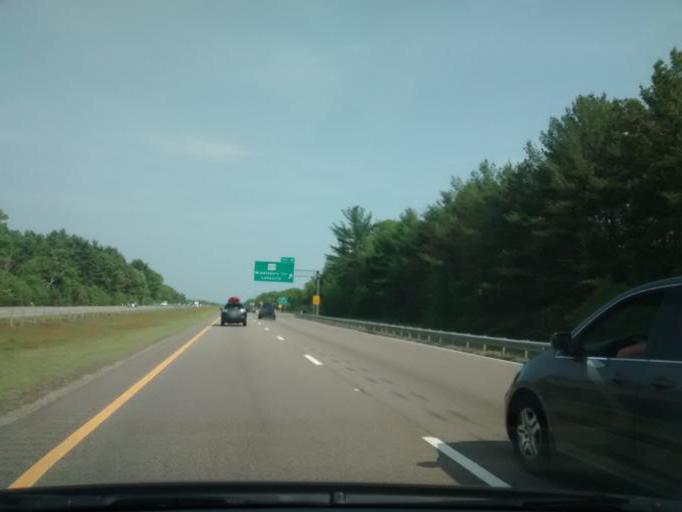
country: US
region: Massachusetts
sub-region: Plymouth County
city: Middleborough Center
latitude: 41.8843
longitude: -70.9259
